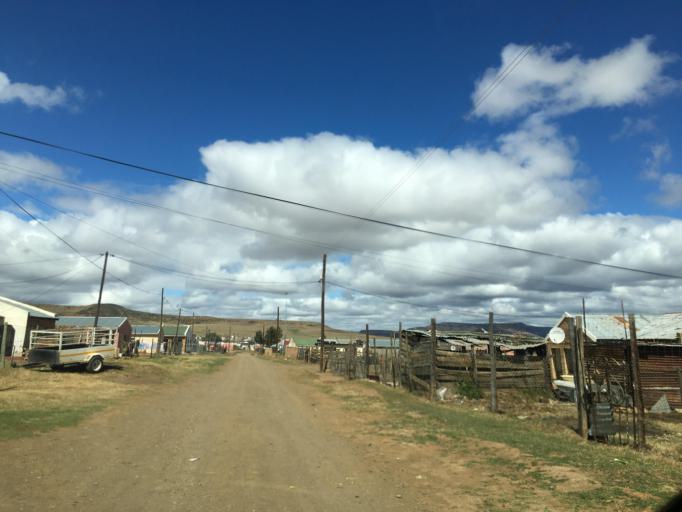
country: ZA
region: Eastern Cape
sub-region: Chris Hani District Municipality
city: Cala
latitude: -31.5324
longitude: 27.7027
